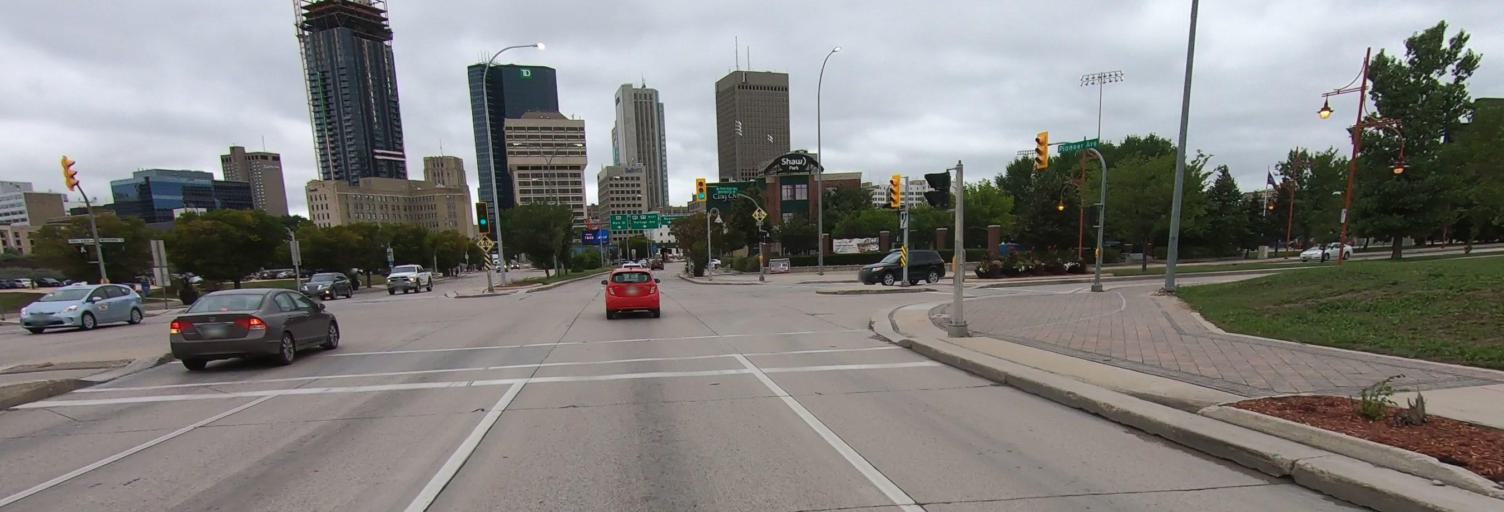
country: CA
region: Manitoba
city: Winnipeg
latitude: 49.8921
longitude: -97.1321
